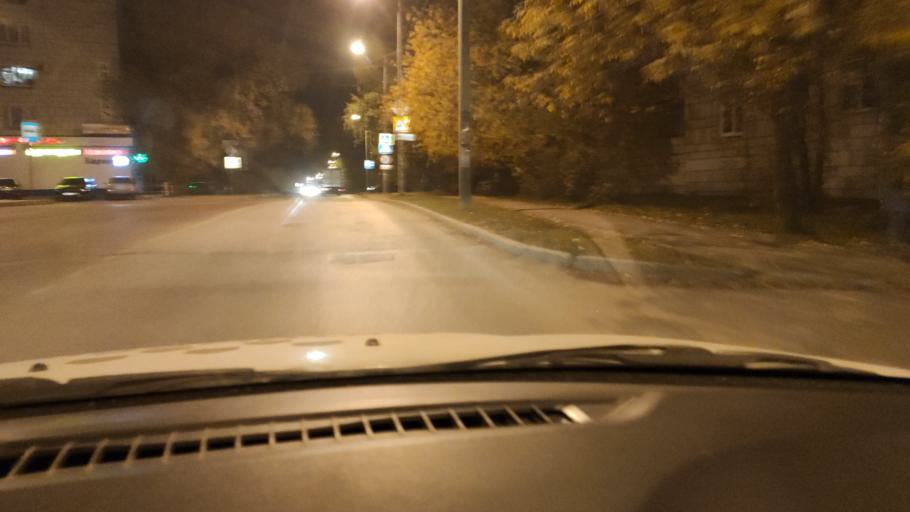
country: RU
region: Perm
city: Perm
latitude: 57.9837
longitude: 56.2855
